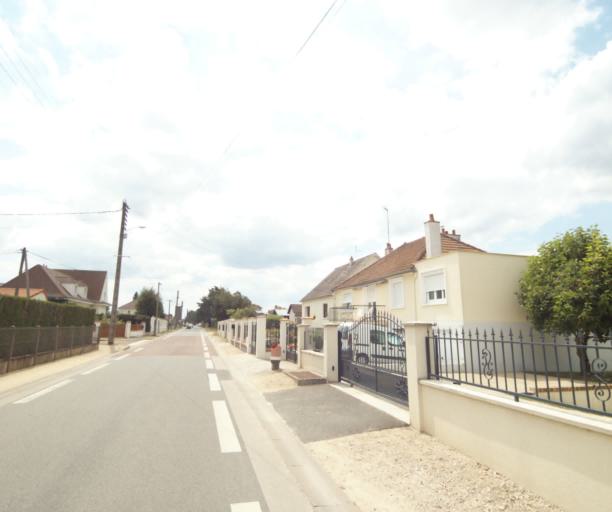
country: FR
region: Centre
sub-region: Departement du Loiret
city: Saint-Hilaire-Saint-Mesmin
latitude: 47.8652
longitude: 1.8456
